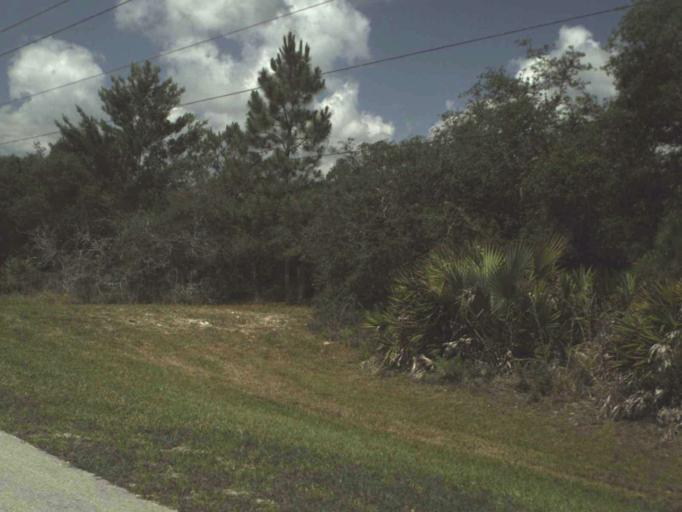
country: US
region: Florida
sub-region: Volusia County
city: Samsula-Spruce Creek
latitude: 28.9636
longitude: -81.0883
